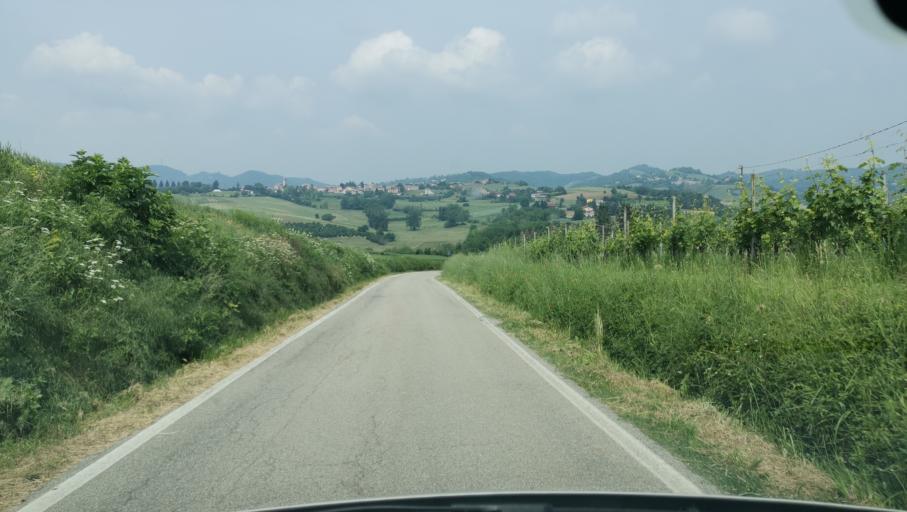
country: IT
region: Piedmont
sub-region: Provincia di Alessandria
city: Castelletto Merli
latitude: 45.0596
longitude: 8.2446
